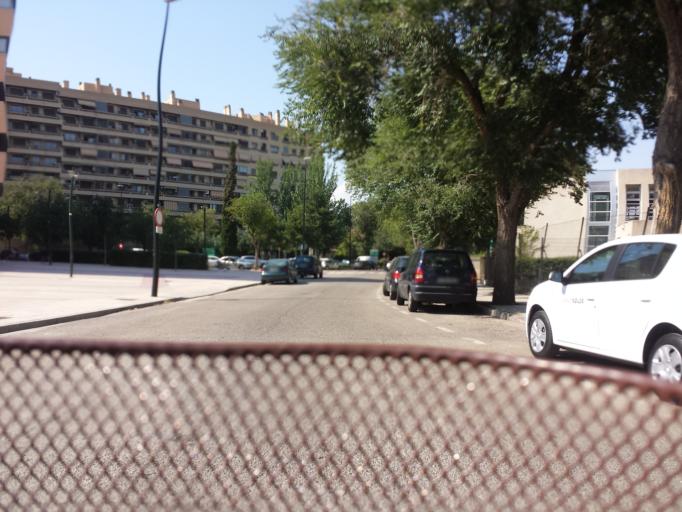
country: ES
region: Aragon
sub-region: Provincia de Zaragoza
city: Zaragoza
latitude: 41.6401
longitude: -0.8626
